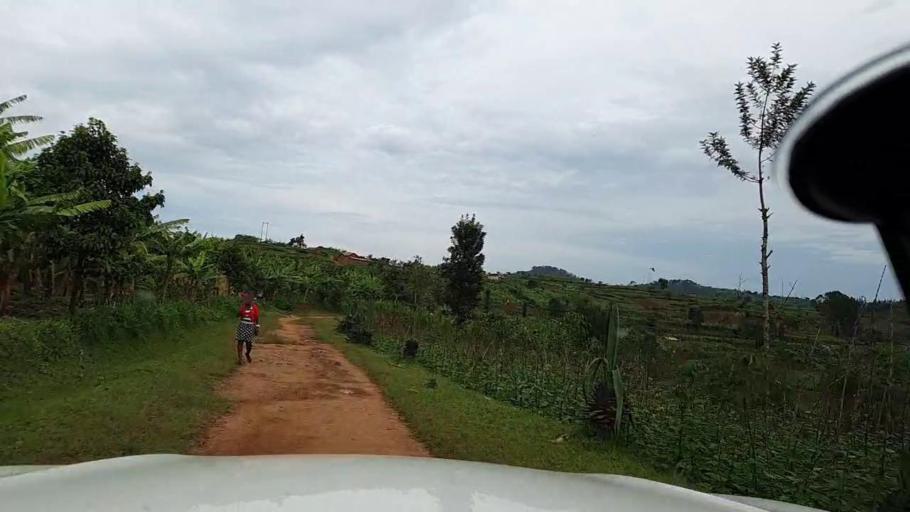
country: RW
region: Southern Province
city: Gitarama
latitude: -2.1158
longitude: 29.6422
